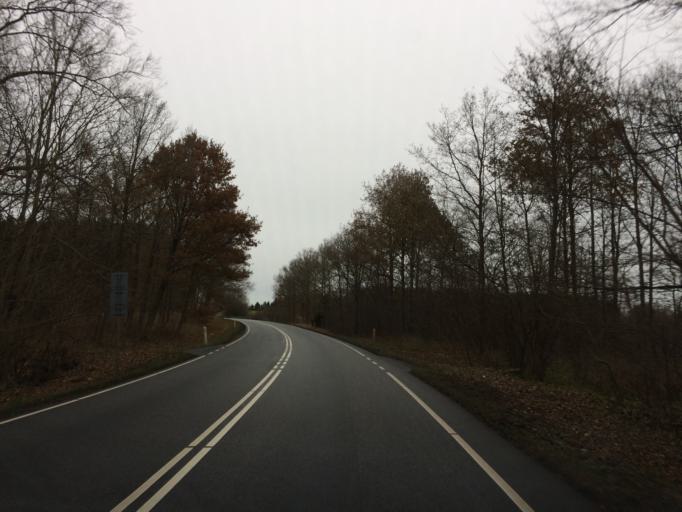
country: DK
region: Zealand
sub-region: Holbaek Kommune
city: Jyderup
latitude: 55.6134
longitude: 11.3896
